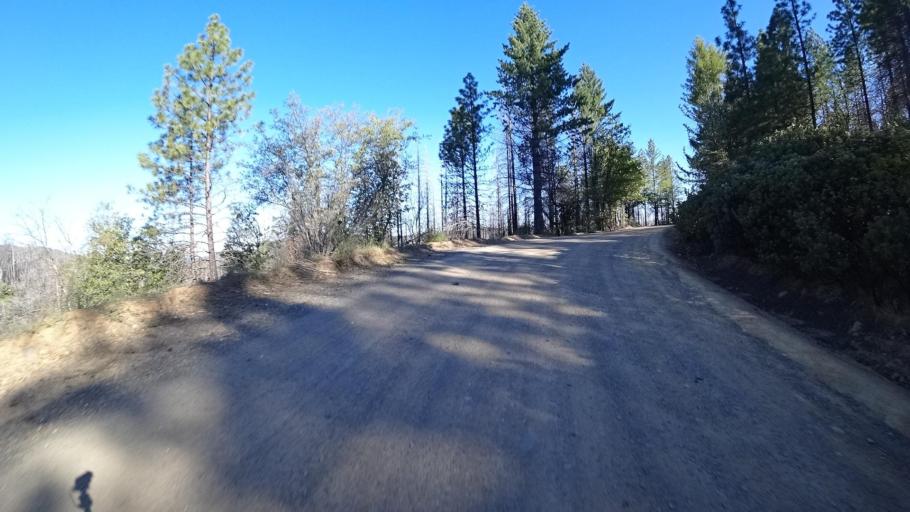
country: US
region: California
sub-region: Lake County
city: Upper Lake
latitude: 39.3338
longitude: -122.9575
